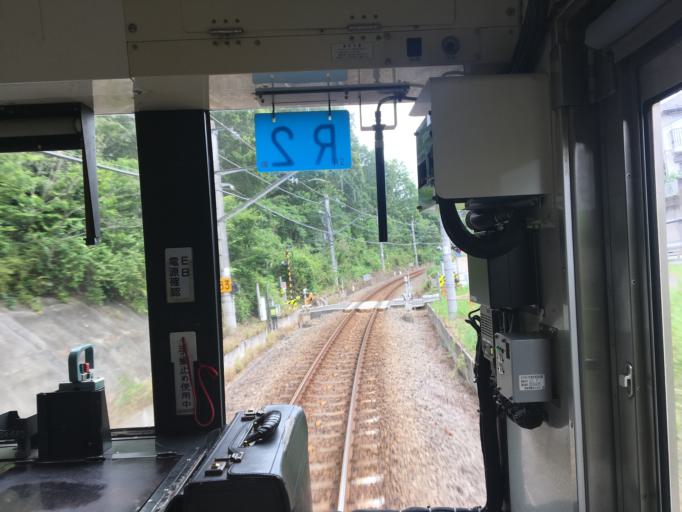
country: JP
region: Kanagawa
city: Zama
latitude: 35.5636
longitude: 139.3558
